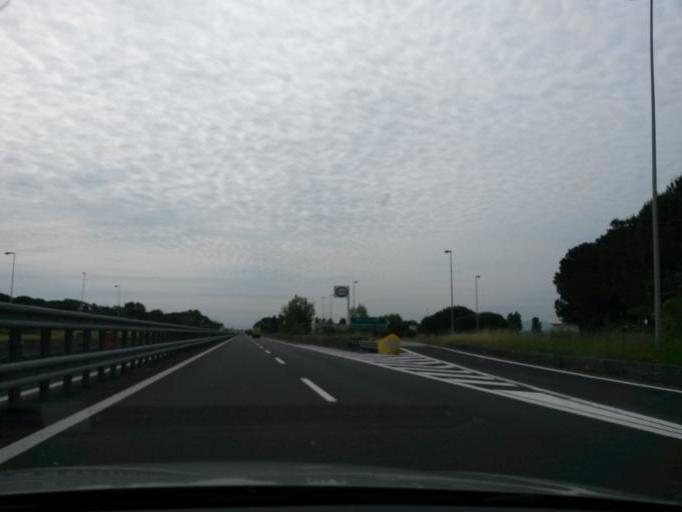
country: IT
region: Tuscany
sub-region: Province of Pisa
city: Pisa
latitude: 43.6703
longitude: 10.3572
